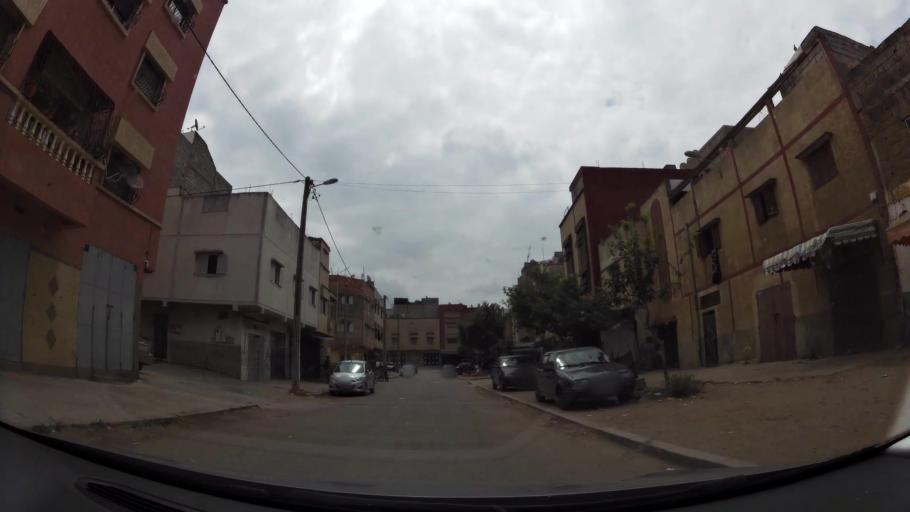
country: MA
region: Rabat-Sale-Zemmour-Zaer
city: Sale
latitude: 34.0611
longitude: -6.7860
